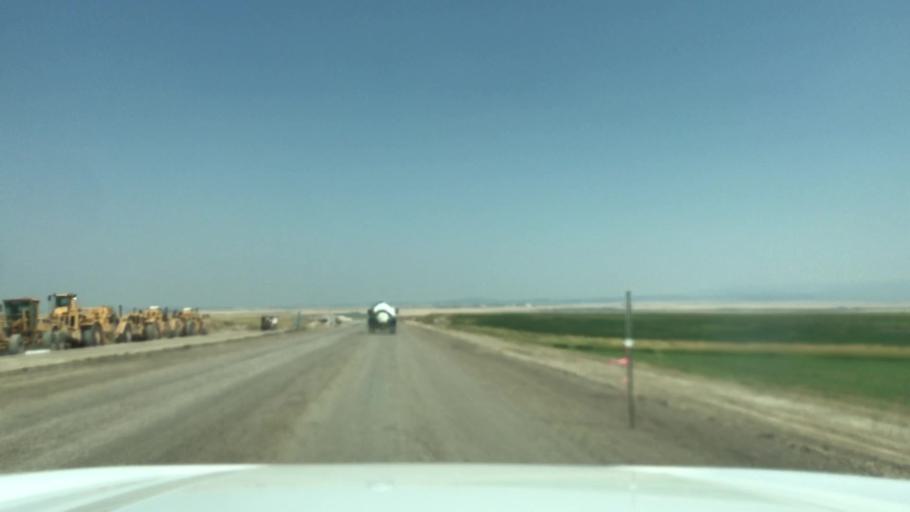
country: US
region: Montana
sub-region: Fergus County
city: Lewistown
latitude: 46.9989
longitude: -109.8177
